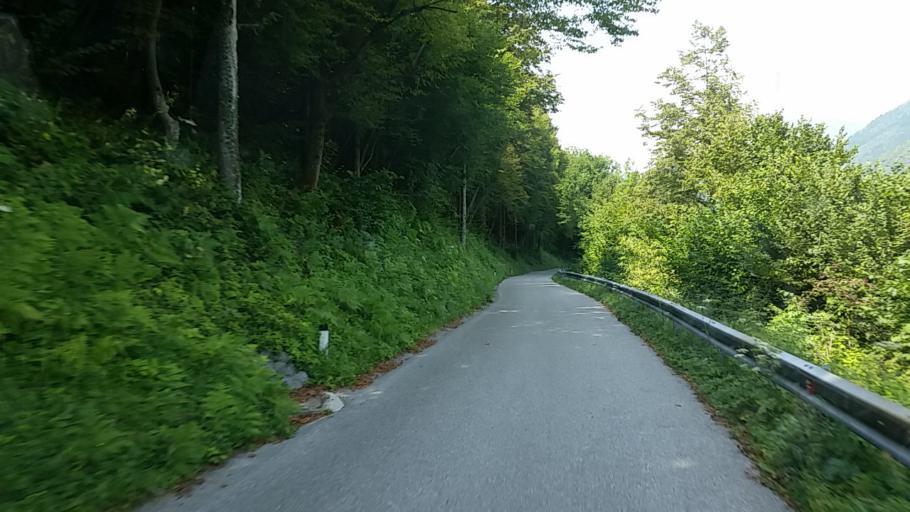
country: SI
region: Tolmin
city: Tolmin
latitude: 46.1361
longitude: 13.7746
